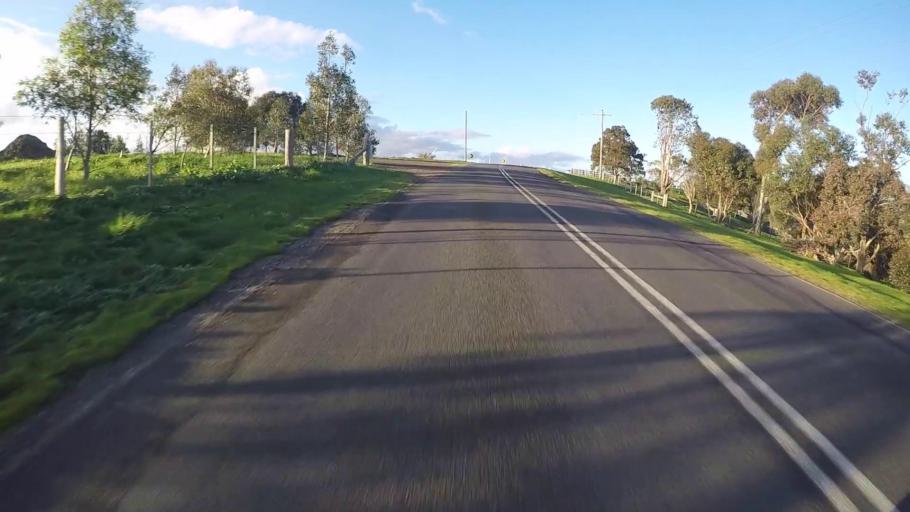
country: AU
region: Victoria
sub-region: Greater Geelong
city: Wandana Heights
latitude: -38.1437
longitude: 144.1897
